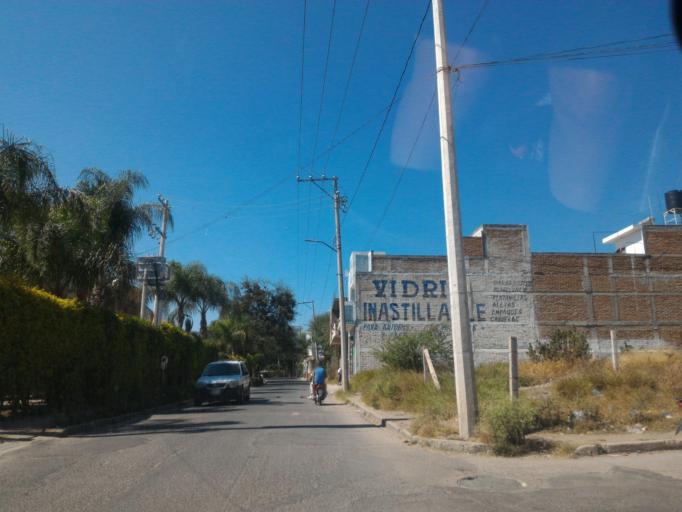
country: MX
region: Guanajuato
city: San Francisco del Rincon
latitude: 21.0372
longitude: -101.8723
